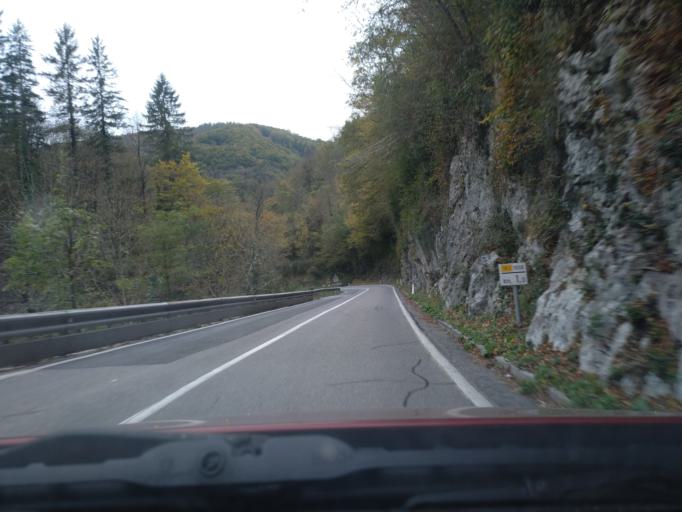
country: SI
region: Tolmin
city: Tolmin
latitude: 46.1436
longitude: 13.7158
